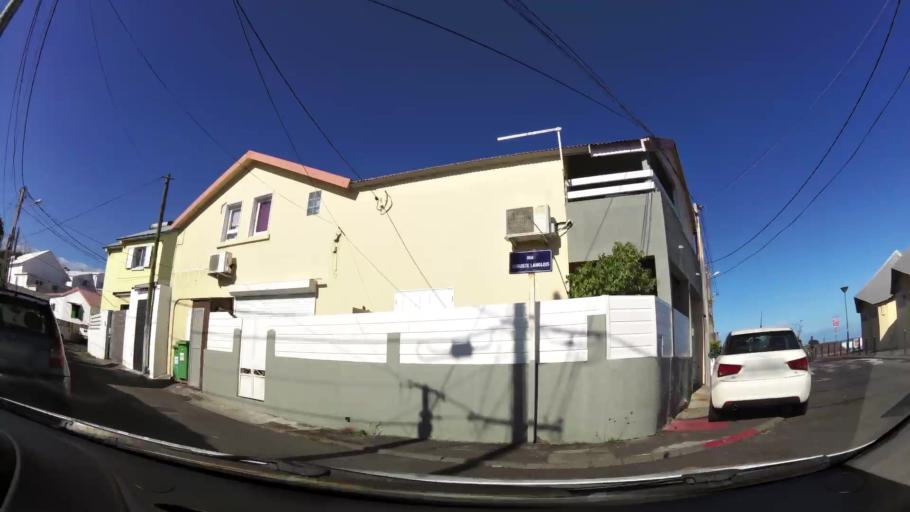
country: RE
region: Reunion
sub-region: Reunion
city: Saint-Pierre
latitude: -21.3469
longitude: 55.4807
